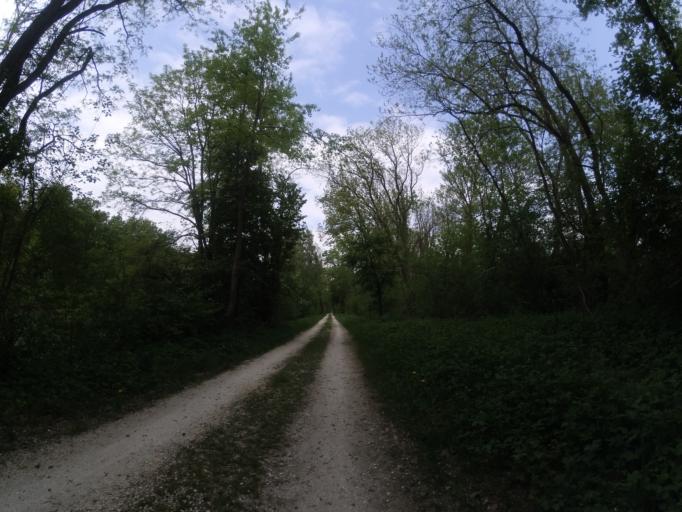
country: DE
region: Bavaria
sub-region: Swabia
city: Neu-Ulm
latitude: 48.3641
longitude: 10.0001
